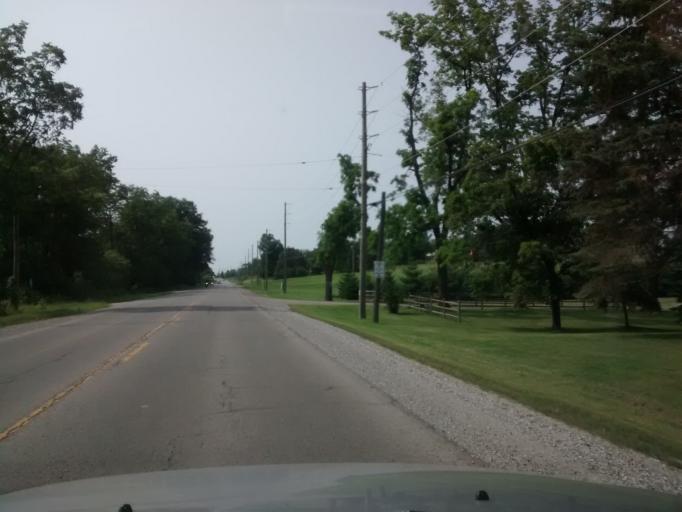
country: CA
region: Ontario
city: Ancaster
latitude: 43.0435
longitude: -79.9051
